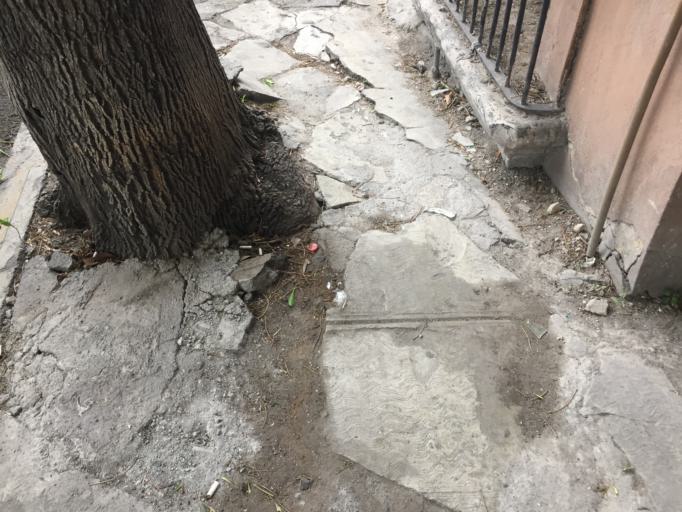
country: MX
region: Nuevo Leon
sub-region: Monterrey
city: Monterrey
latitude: 25.6815
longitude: -100.3064
